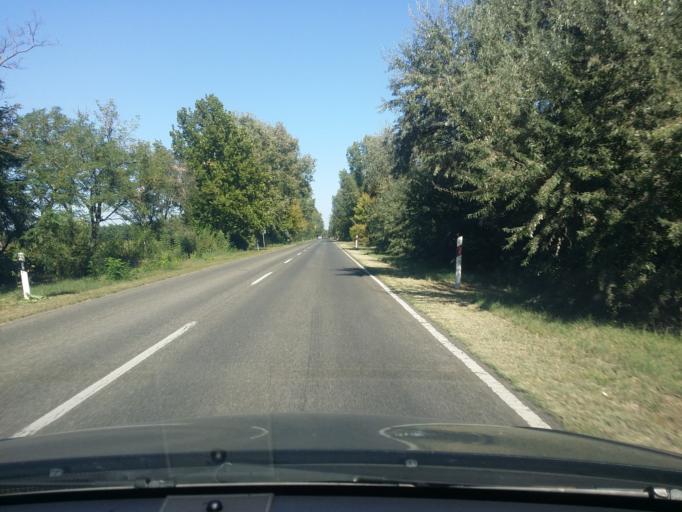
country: HU
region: Csongrad
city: Kistelek
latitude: 46.5007
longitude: 19.9650
